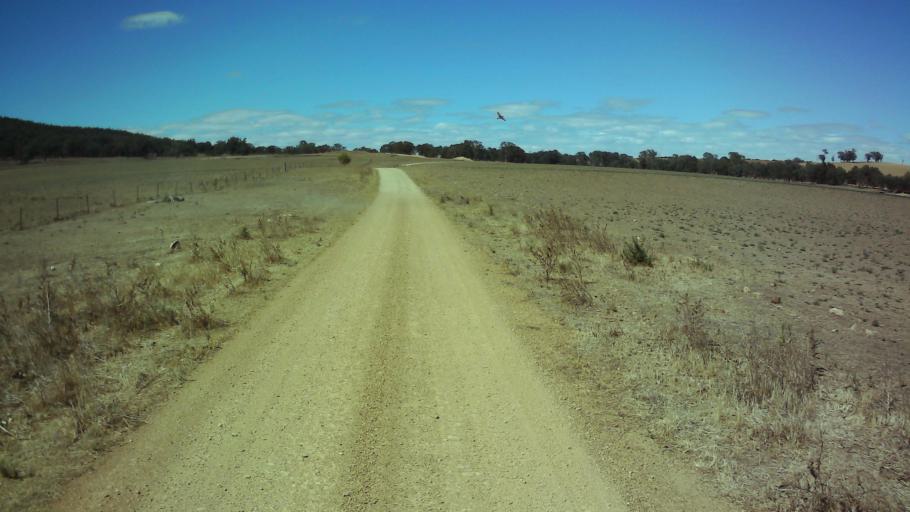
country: AU
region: New South Wales
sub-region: Weddin
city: Grenfell
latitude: -34.0392
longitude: 148.4318
